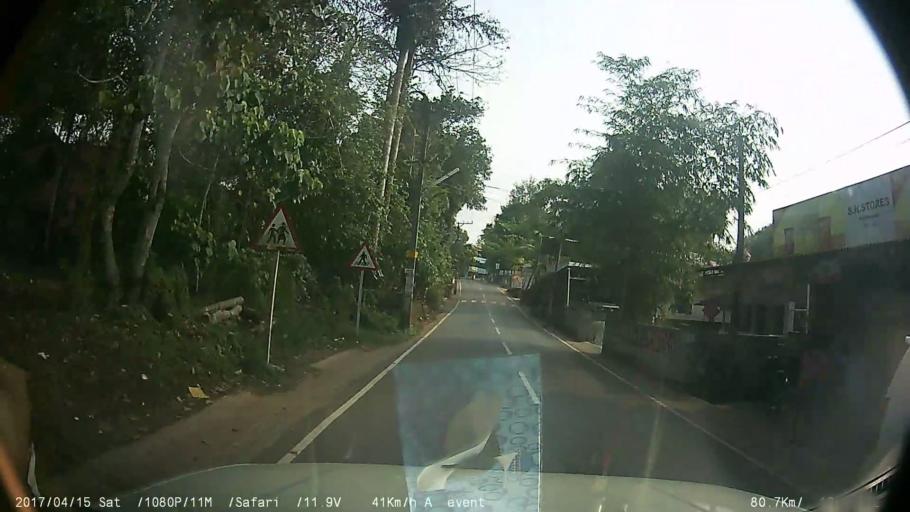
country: IN
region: Kerala
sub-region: Kottayam
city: Kottayam
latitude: 9.6546
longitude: 76.5257
